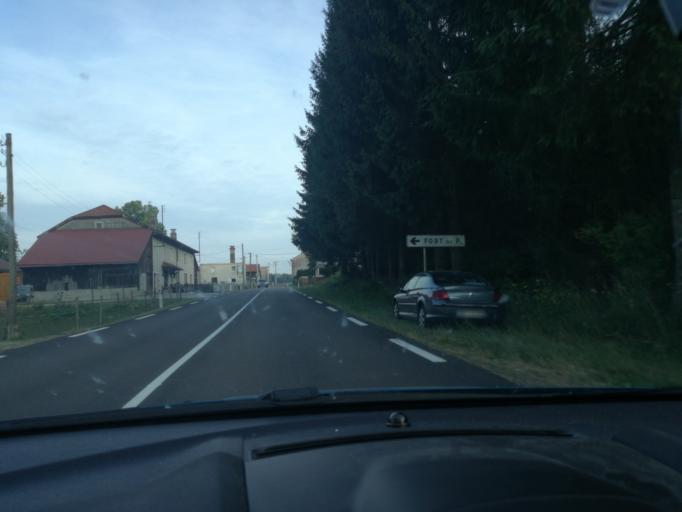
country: FR
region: Franche-Comte
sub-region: Departement du Jura
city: Morbier
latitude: 46.6092
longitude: 5.9614
